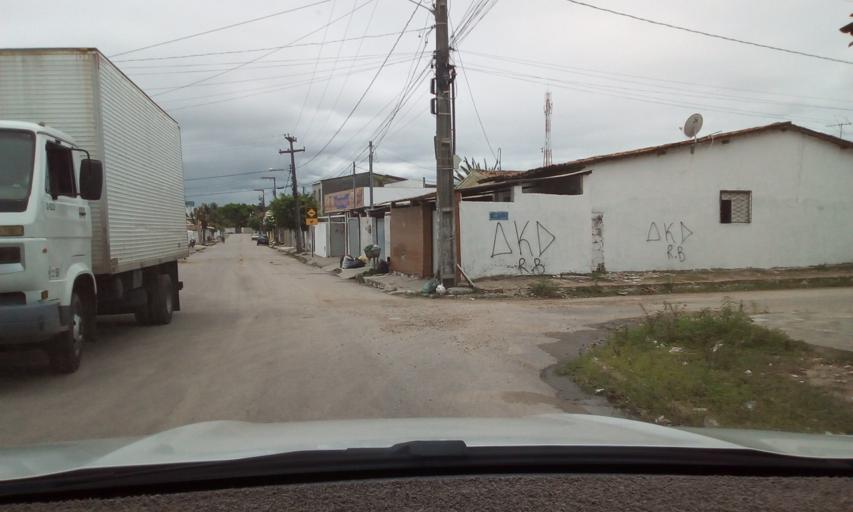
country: BR
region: Paraiba
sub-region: Conde
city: Conde
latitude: -7.2127
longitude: -34.8378
